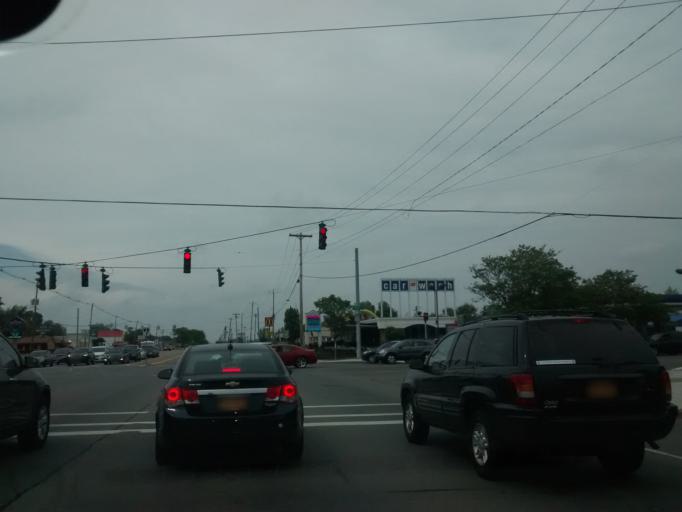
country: US
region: New York
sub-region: Erie County
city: Amherst
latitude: 42.9905
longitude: -78.8225
